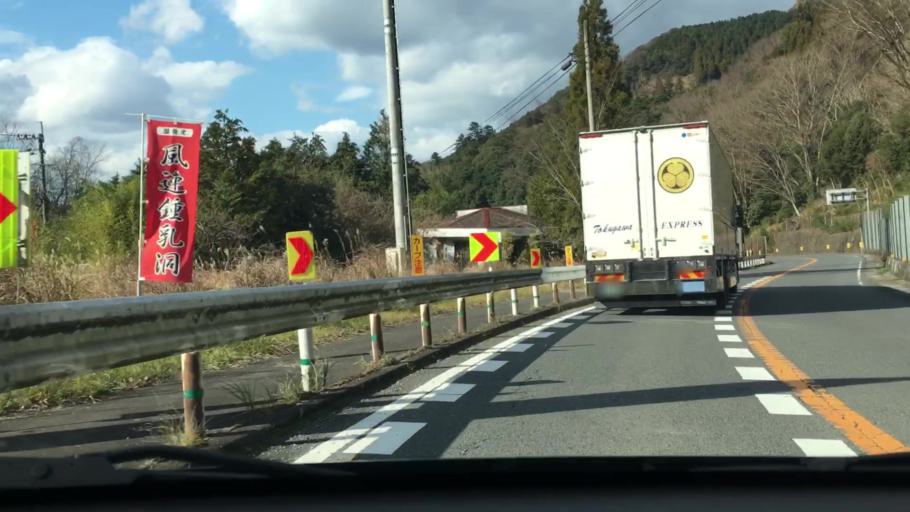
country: JP
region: Oita
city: Usuki
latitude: 32.9986
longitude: 131.7519
